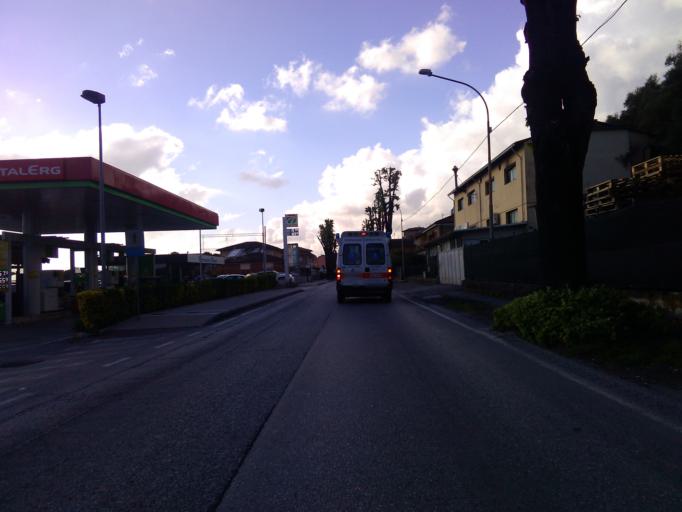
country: IT
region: Tuscany
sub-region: Provincia di Lucca
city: Pietrasanta
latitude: 43.9523
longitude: 10.2377
